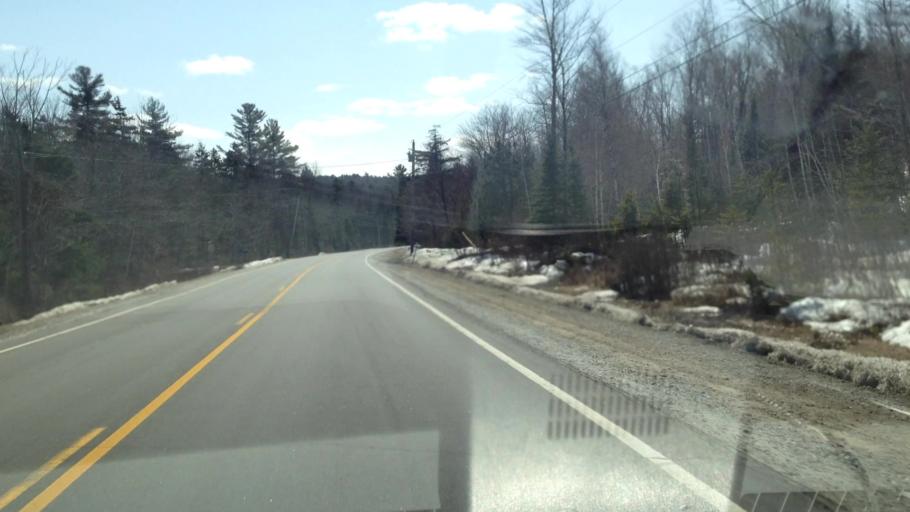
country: US
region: New Hampshire
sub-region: Merrimack County
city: Wilmot
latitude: 43.4707
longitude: -71.9618
